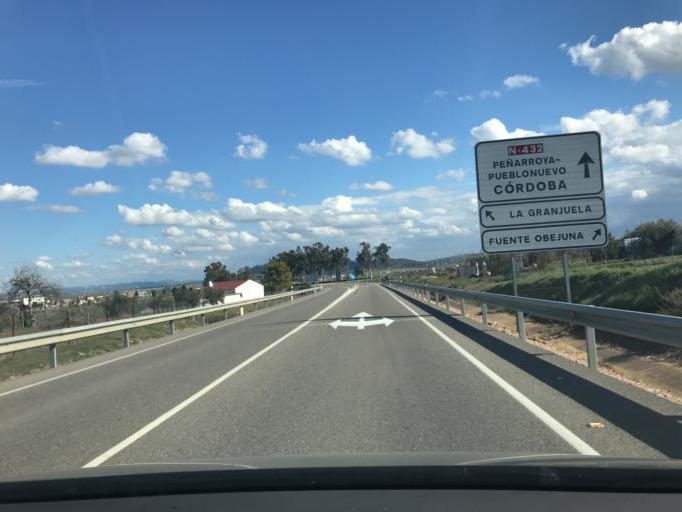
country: ES
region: Andalusia
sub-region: Province of Cordoba
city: Fuente Obejuna
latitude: 38.2748
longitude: -5.4138
